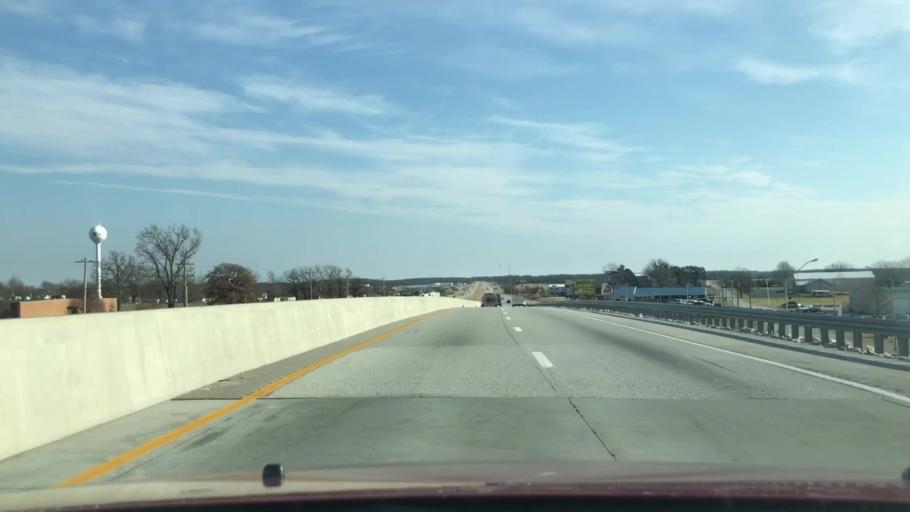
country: US
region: Missouri
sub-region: Webster County
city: Rogersville
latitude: 37.1107
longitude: -93.0564
